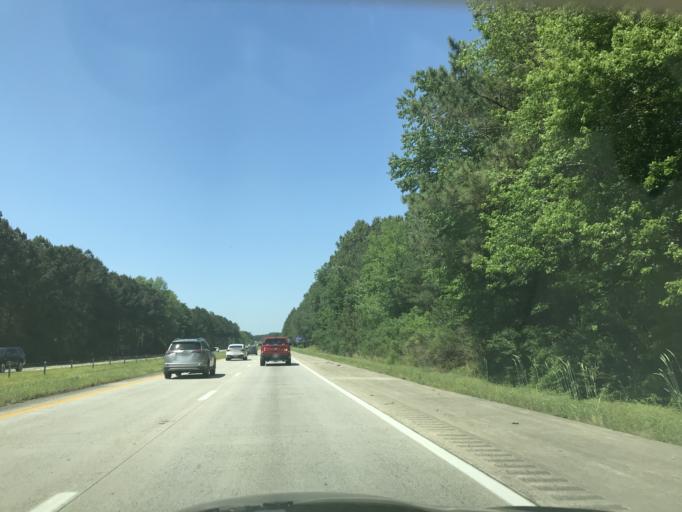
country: US
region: North Carolina
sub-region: Johnston County
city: Benson
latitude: 35.5033
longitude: -78.5545
